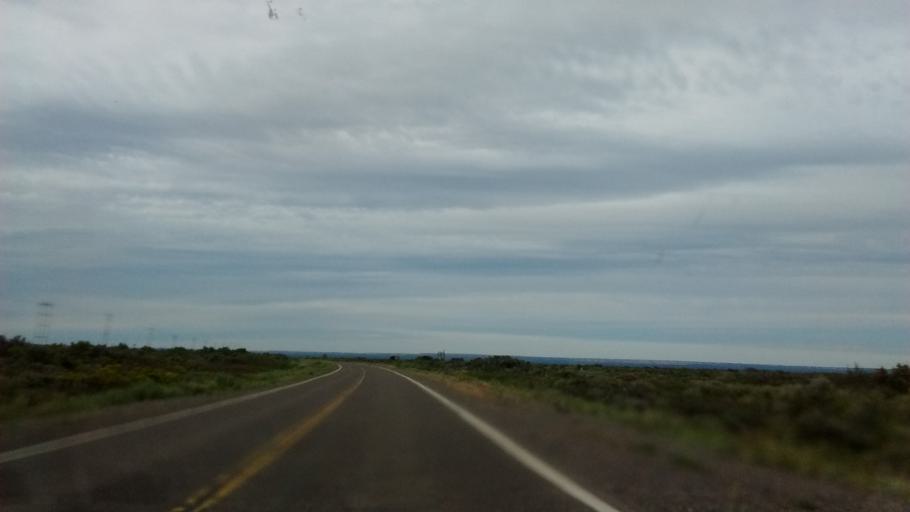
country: AR
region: Rio Negro
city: Catriel
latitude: -37.9810
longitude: -67.9080
